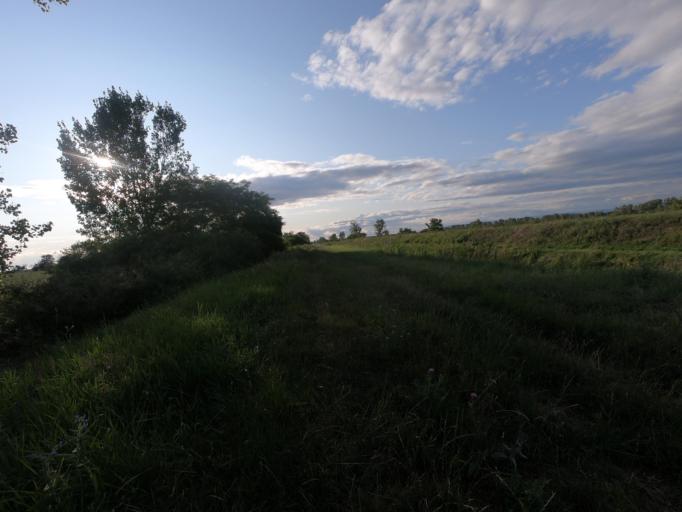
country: HU
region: Heves
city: Szihalom
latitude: 47.7177
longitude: 20.5670
